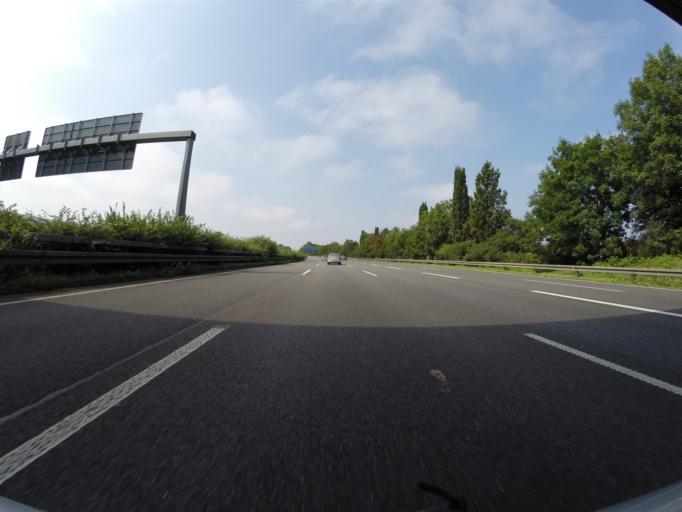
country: DE
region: Hesse
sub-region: Regierungsbezirk Kassel
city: Lohfelden
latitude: 51.2722
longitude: 9.5223
